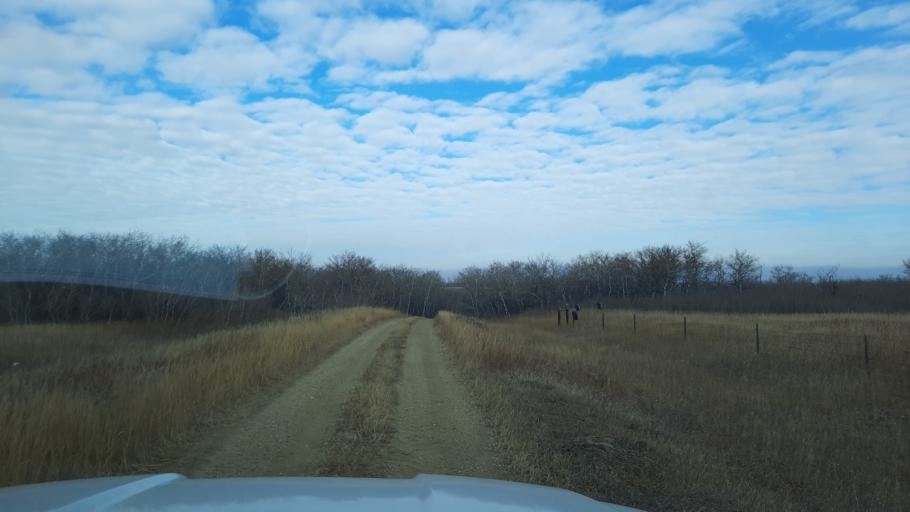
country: CA
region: Saskatchewan
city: Pilot Butte
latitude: 50.7734
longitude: -104.2157
